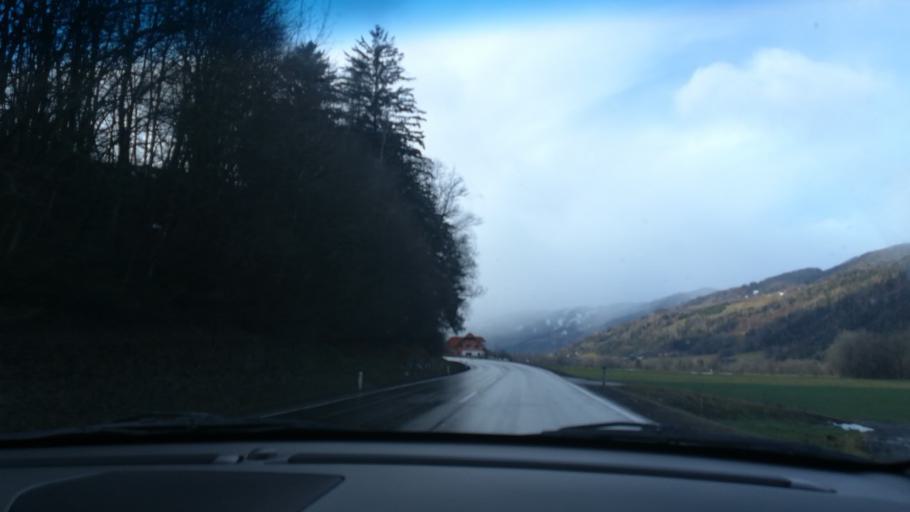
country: AT
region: Styria
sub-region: Politischer Bezirk Murtal
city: Poels
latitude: 47.2036
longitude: 14.5545
